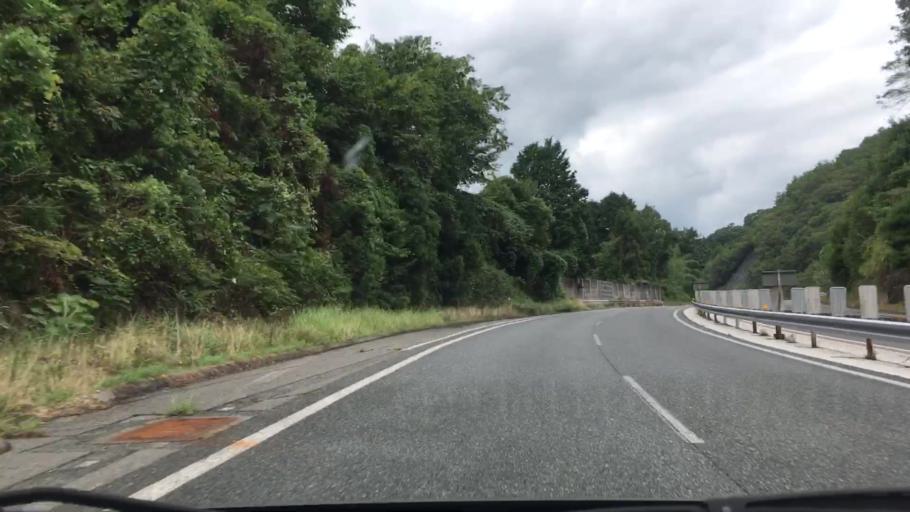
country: JP
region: Okayama
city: Niimi
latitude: 35.0087
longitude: 133.5091
